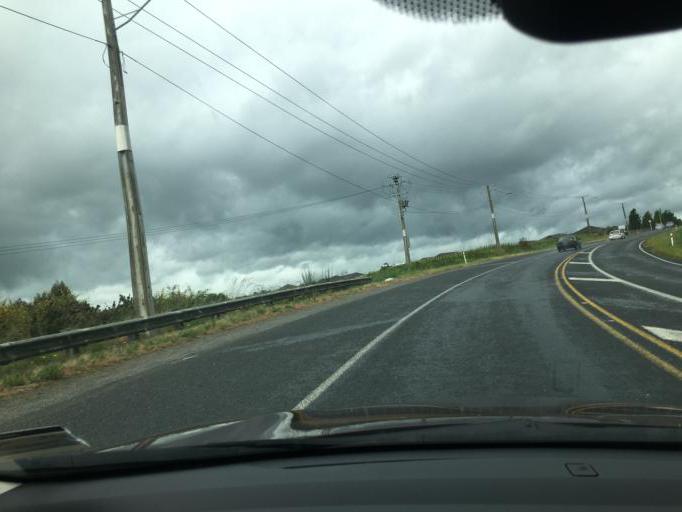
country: NZ
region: Waikato
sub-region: Waipa District
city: Cambridge
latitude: -37.8992
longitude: 175.4576
